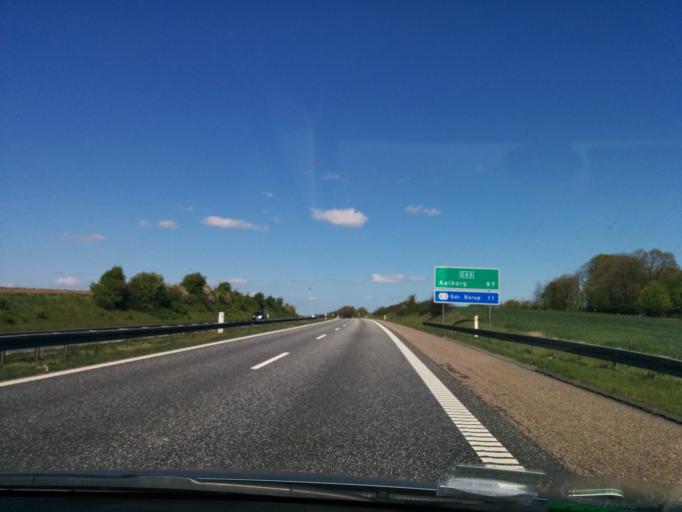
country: DK
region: Central Jutland
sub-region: Favrskov Kommune
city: Hadsten
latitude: 56.3266
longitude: 10.1233
